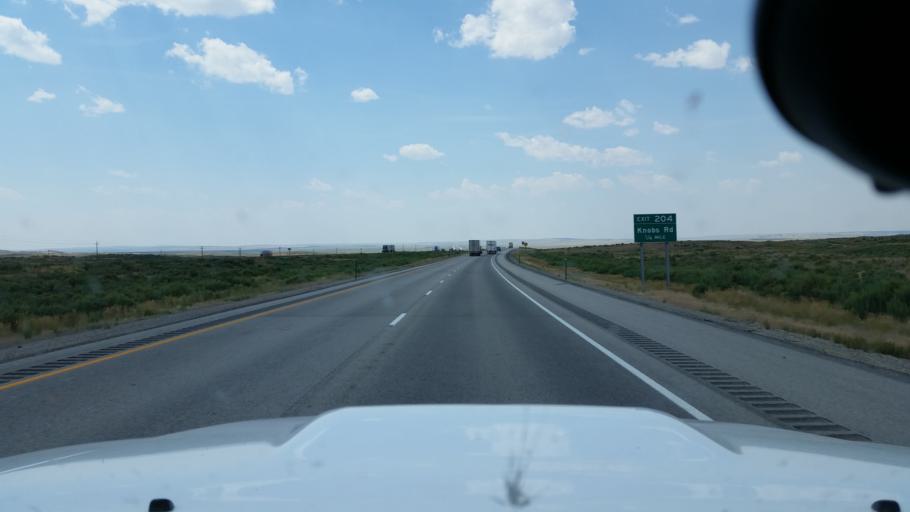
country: US
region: Wyoming
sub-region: Carbon County
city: Rawlins
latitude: 41.7869
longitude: -107.4026
